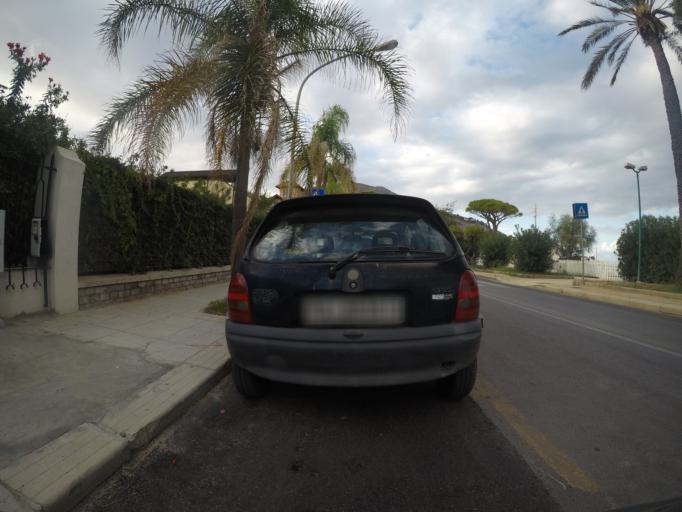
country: IT
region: Sicily
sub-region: Palermo
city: Palermo
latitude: 38.2005
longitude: 13.3275
